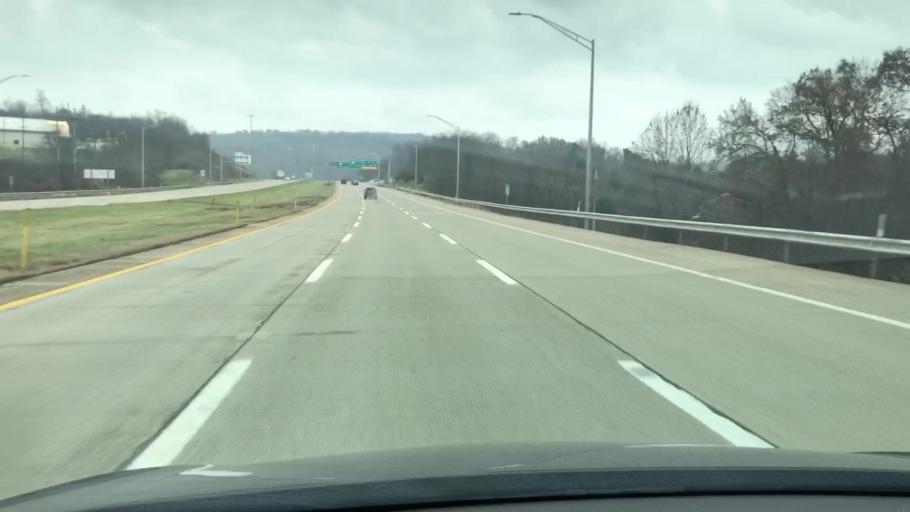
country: US
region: Pennsylvania
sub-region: Westmoreland County
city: New Stanton
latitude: 40.2316
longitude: -79.6002
